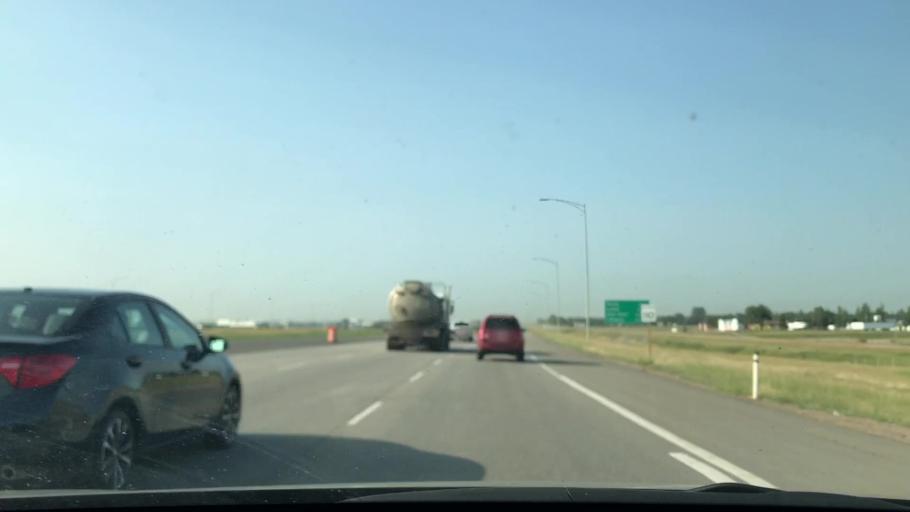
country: CA
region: Alberta
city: Beaumont
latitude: 53.3869
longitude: -113.5167
